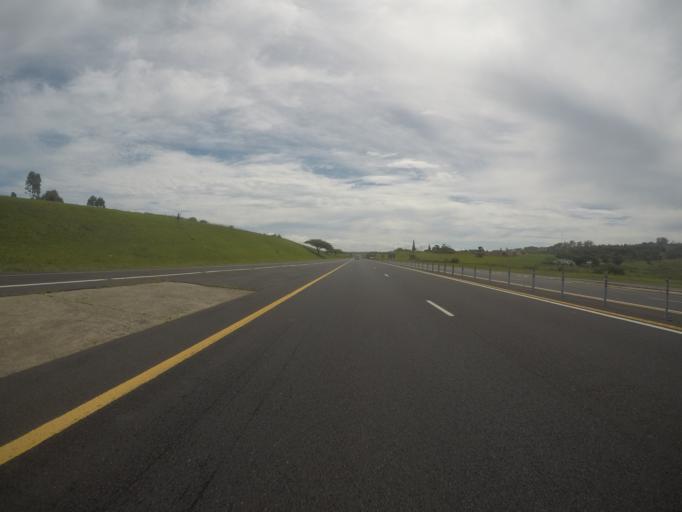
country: ZA
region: KwaZulu-Natal
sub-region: iLembe District Municipality
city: Mandeni
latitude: -29.0737
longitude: 31.6174
